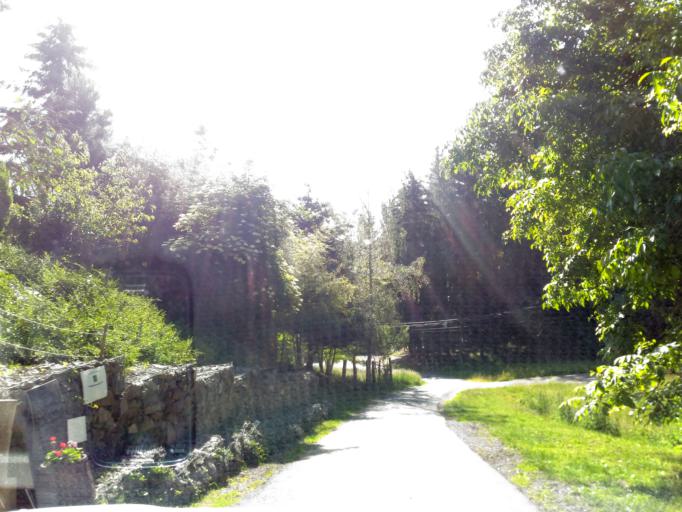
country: HU
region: Baranya
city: Hosszuheteny
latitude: 46.2110
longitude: 18.3680
